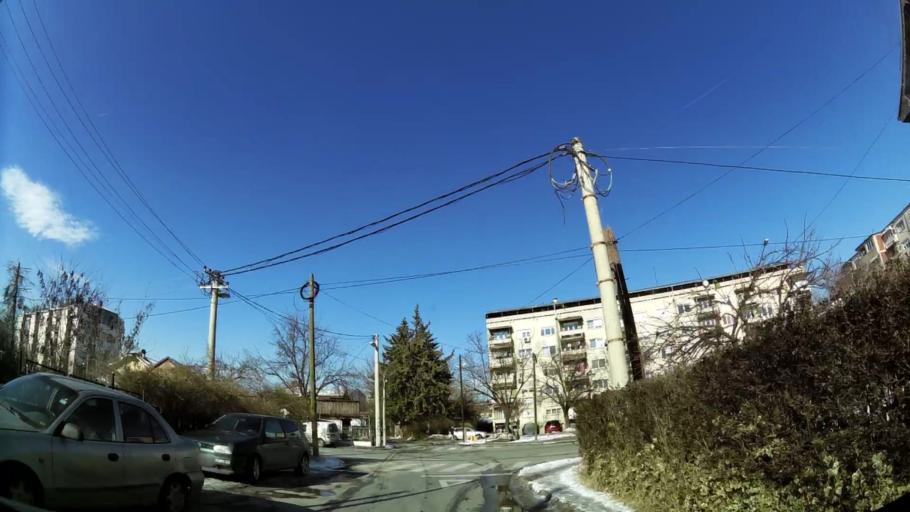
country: MK
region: Saraj
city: Saraj
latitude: 42.0085
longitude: 21.3480
